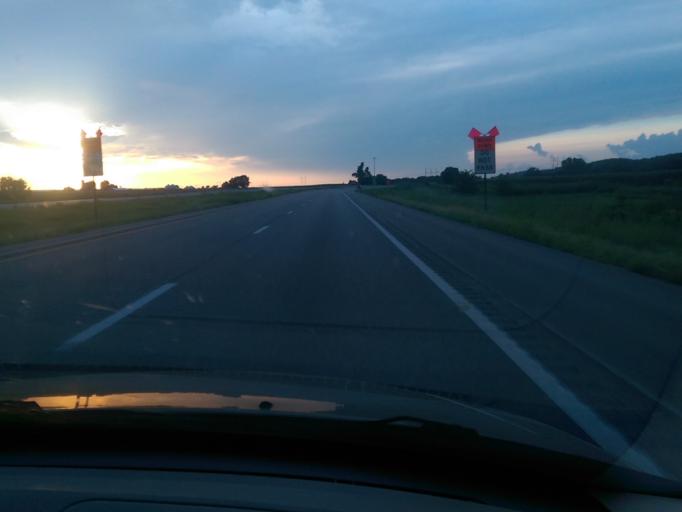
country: US
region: Missouri
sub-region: Atchison County
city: Rock Port
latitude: 40.3477
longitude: -95.5097
